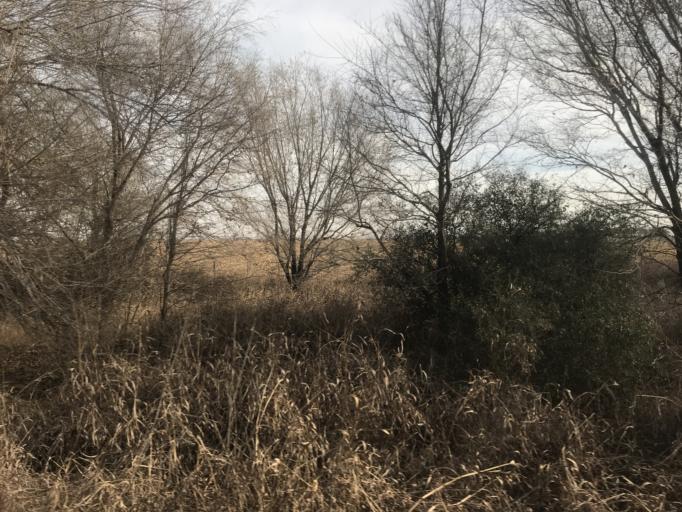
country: AR
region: Cordoba
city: Pilar
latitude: -31.7184
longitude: -63.8541
